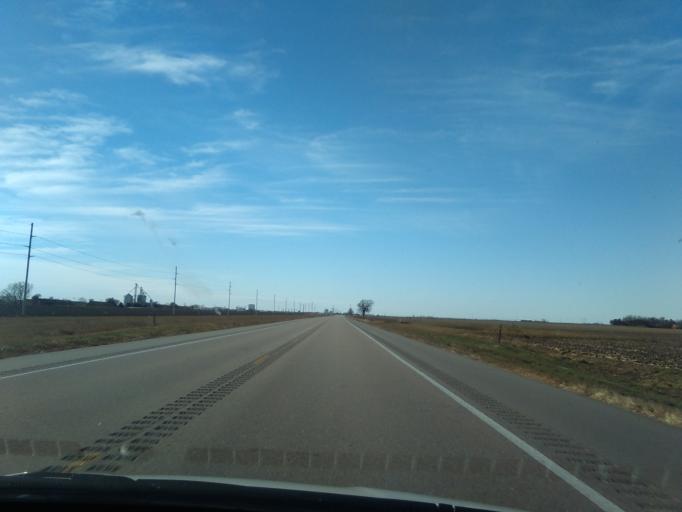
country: US
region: Nebraska
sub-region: Clay County
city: Harvard
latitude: 40.5824
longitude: -98.2105
